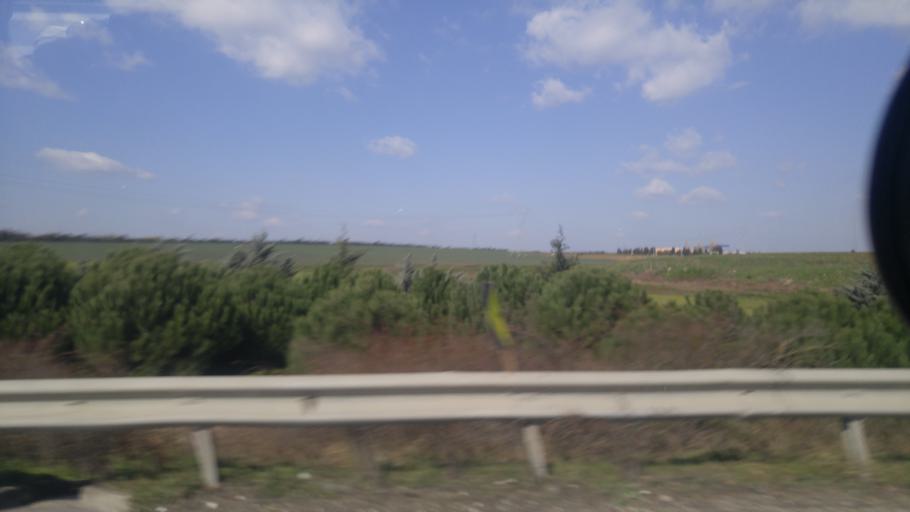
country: TR
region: Istanbul
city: Silivri
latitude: 41.1183
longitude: 28.2071
